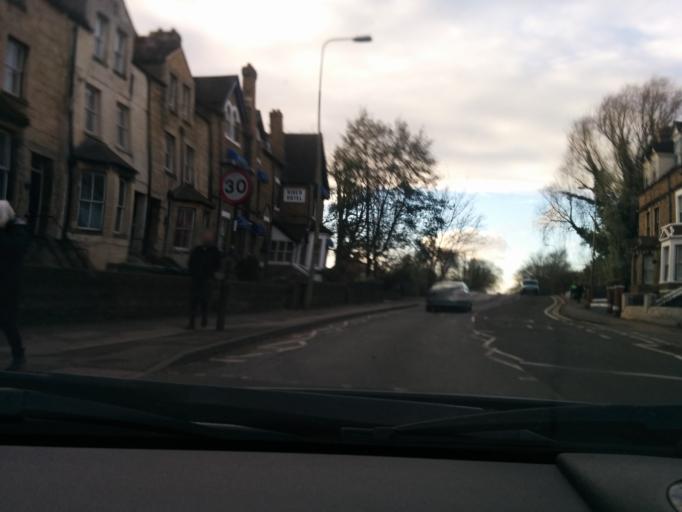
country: GB
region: England
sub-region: Oxfordshire
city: Oxford
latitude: 51.7525
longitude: -1.2714
